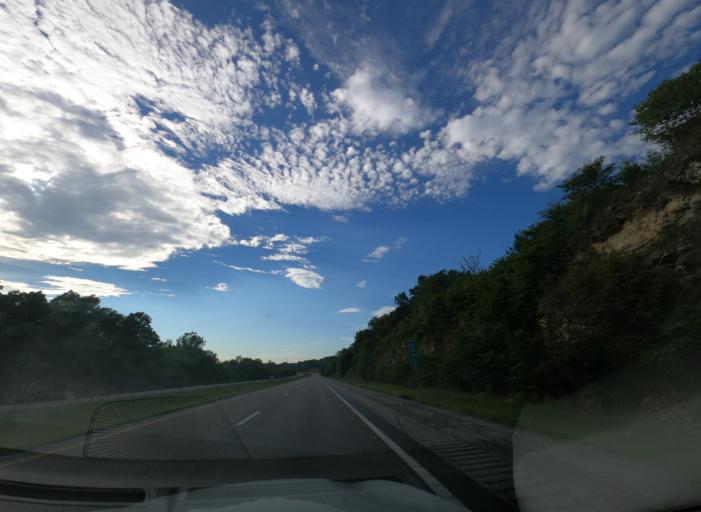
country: US
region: Missouri
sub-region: Jefferson County
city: Crystal City
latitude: 38.1421
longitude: -90.3334
